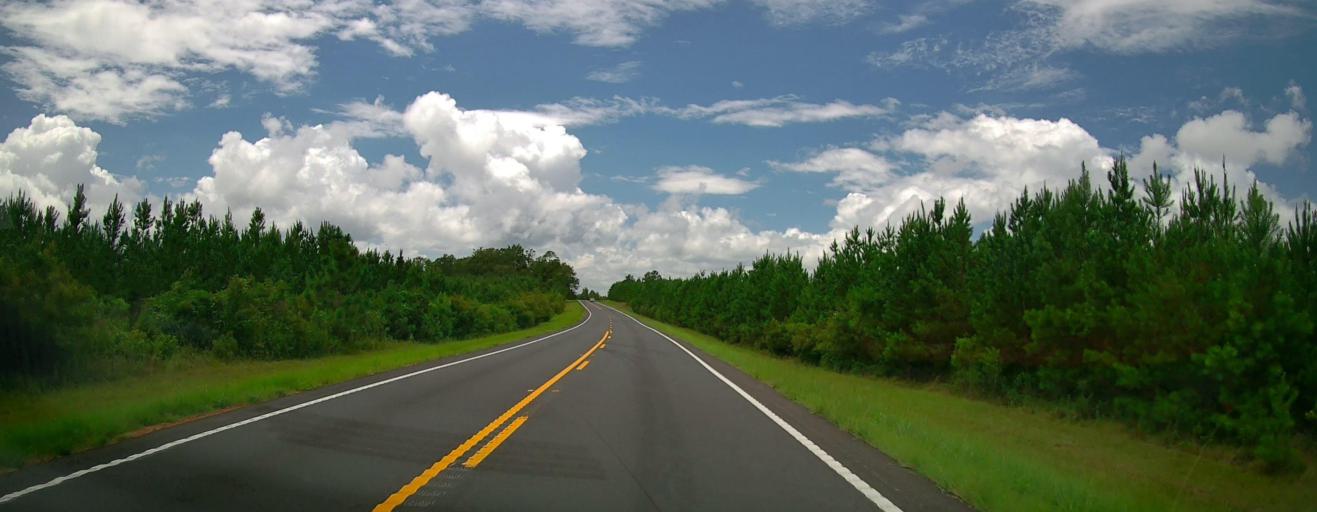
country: US
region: Georgia
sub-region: Dooly County
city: Vienna
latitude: 32.0762
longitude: -83.6213
